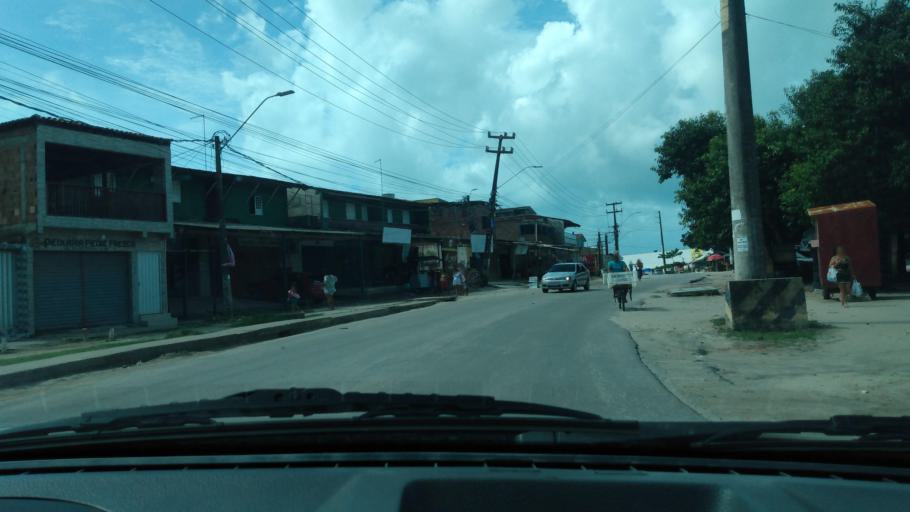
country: BR
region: Pernambuco
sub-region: Cabo De Santo Agostinho
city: Cabo
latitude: -8.3397
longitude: -34.9556
